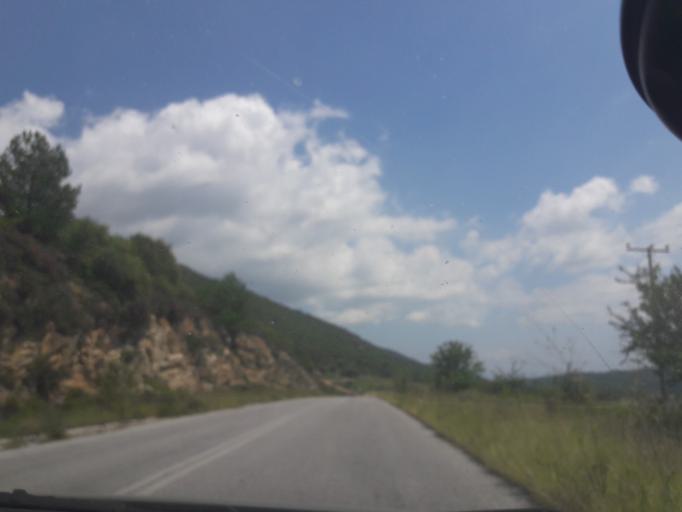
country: GR
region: Central Macedonia
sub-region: Nomos Chalkidikis
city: Polygyros
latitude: 40.3676
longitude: 23.4611
